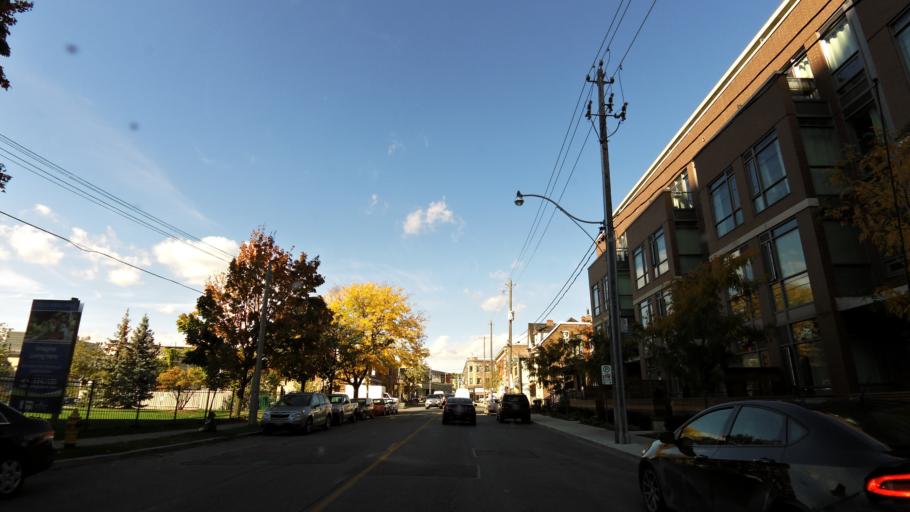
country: CA
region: Ontario
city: Toronto
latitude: 43.6603
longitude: -79.4290
